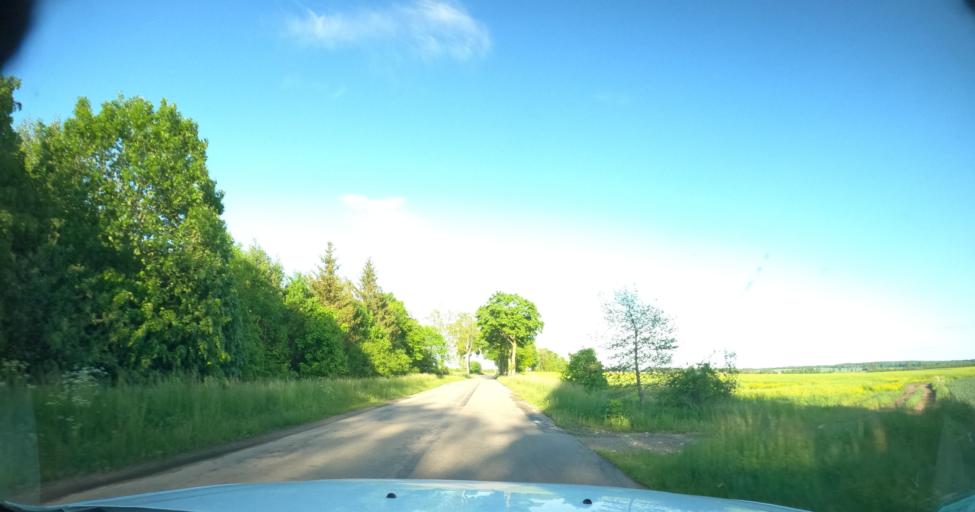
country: PL
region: Warmian-Masurian Voivodeship
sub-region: Powiat braniewski
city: Braniewo
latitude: 54.2793
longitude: 19.9127
